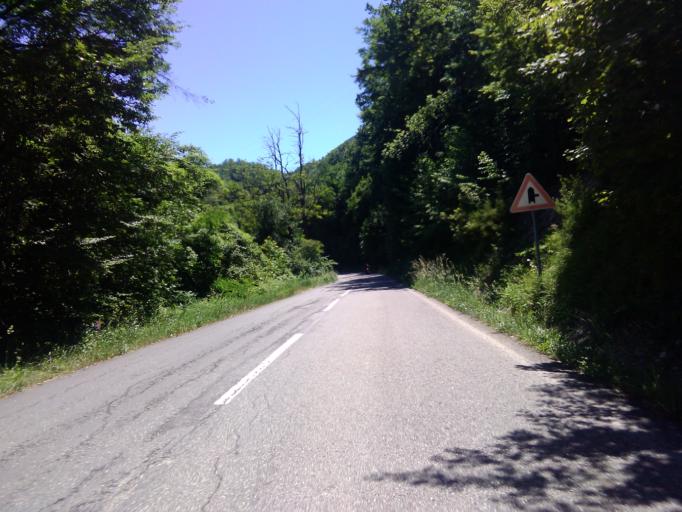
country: IT
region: Emilia-Romagna
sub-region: Provincia di Parma
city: Terenzo
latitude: 44.5799
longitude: 10.0853
